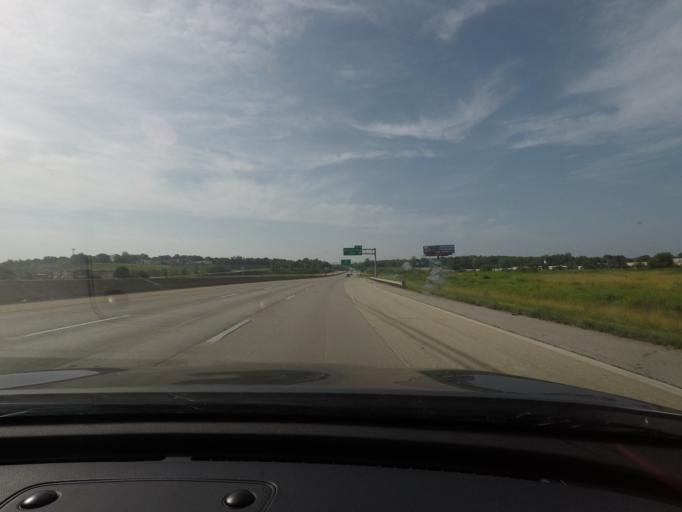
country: US
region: Missouri
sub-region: Saint Louis County
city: Bridgeton
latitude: 38.7858
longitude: -90.4197
